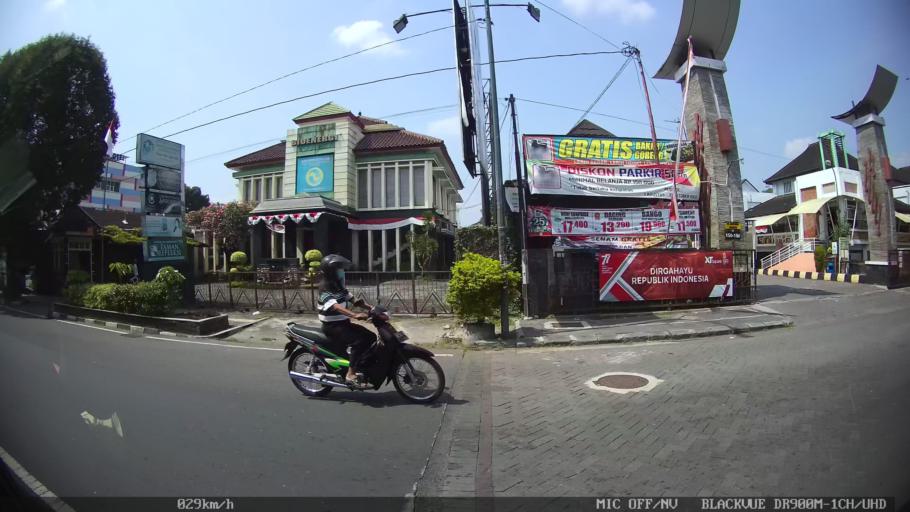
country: ID
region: Daerah Istimewa Yogyakarta
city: Yogyakarta
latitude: -7.8161
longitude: 110.3874
